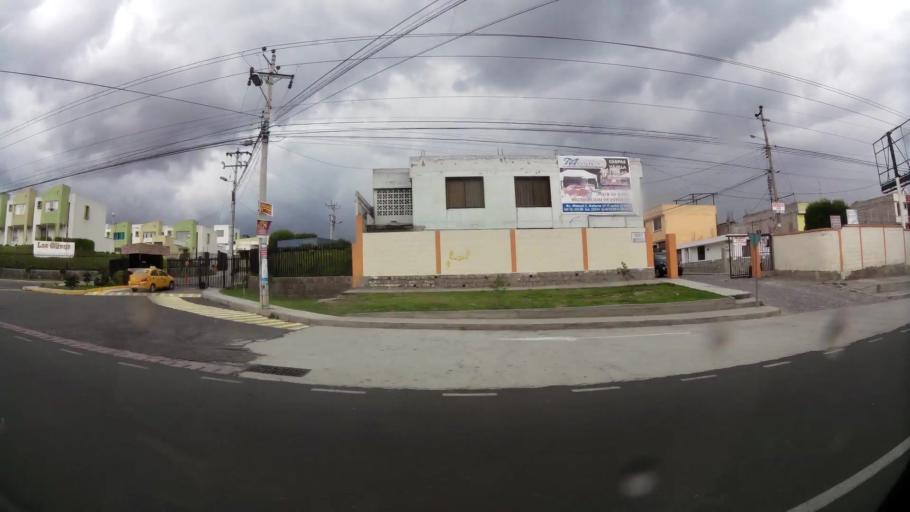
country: EC
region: Pichincha
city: Quito
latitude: -0.0714
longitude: -78.4720
